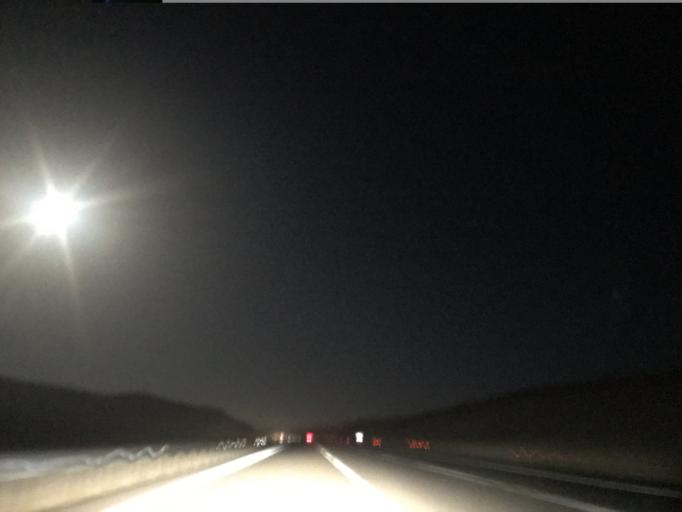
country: TR
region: Nigde
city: Ulukisla
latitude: 37.6430
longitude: 34.3762
